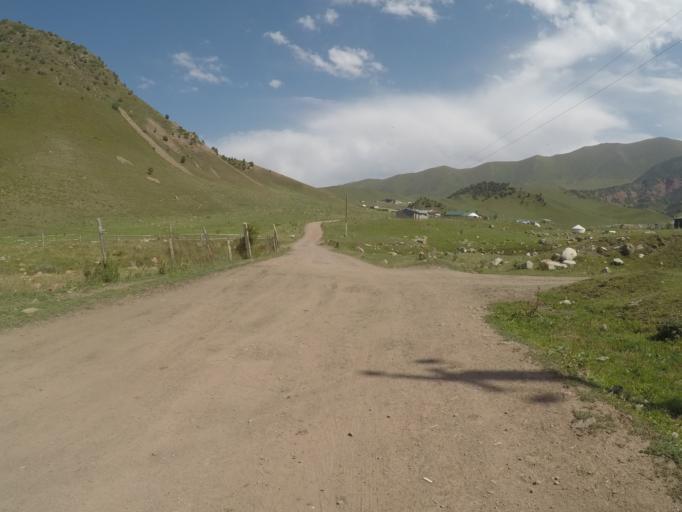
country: KG
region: Chuy
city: Bishkek
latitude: 42.6435
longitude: 74.6163
